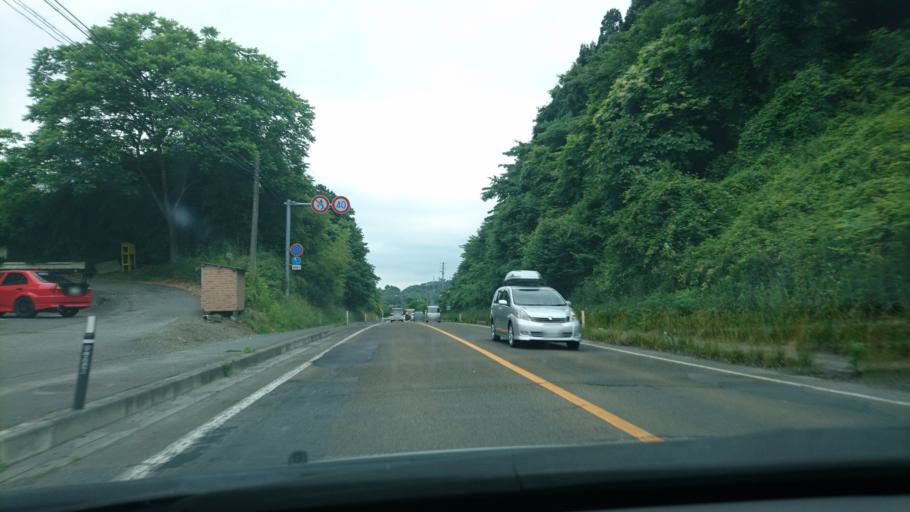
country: JP
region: Miyagi
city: Furukawa
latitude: 38.7271
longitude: 141.0215
